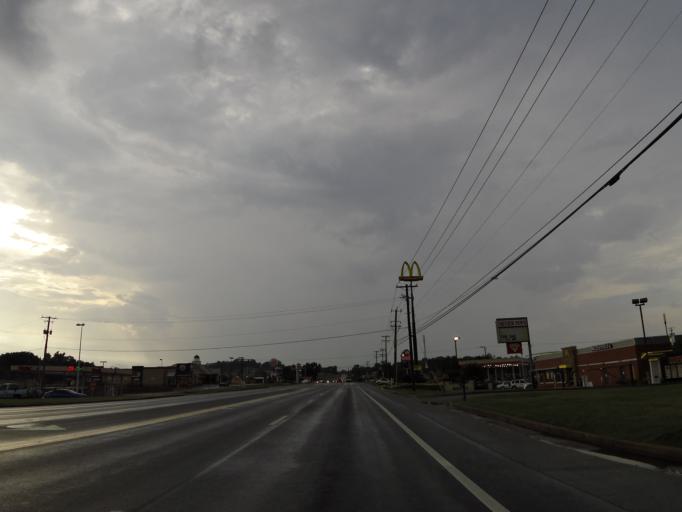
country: US
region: Tennessee
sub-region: Sevier County
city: Seymour
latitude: 35.8696
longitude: -83.7550
